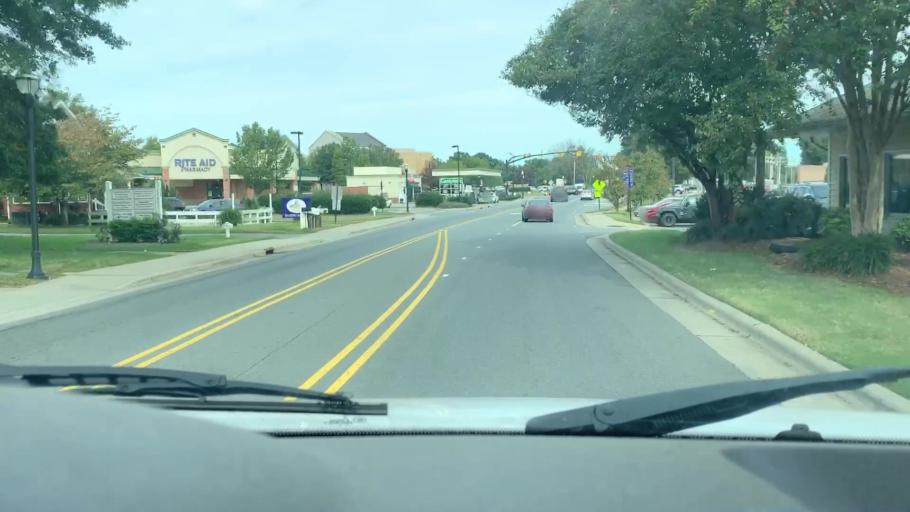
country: US
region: North Carolina
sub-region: Mecklenburg County
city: Cornelius
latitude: 35.4799
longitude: -80.8573
